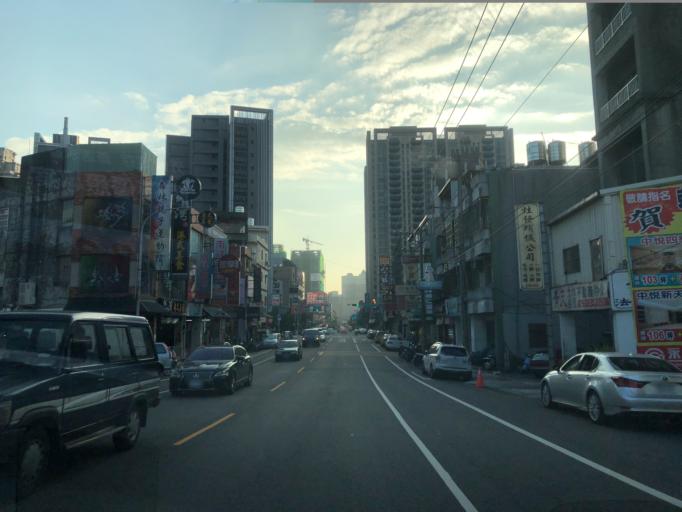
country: TW
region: Taiwan
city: Taoyuan City
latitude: 25.0463
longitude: 121.2970
